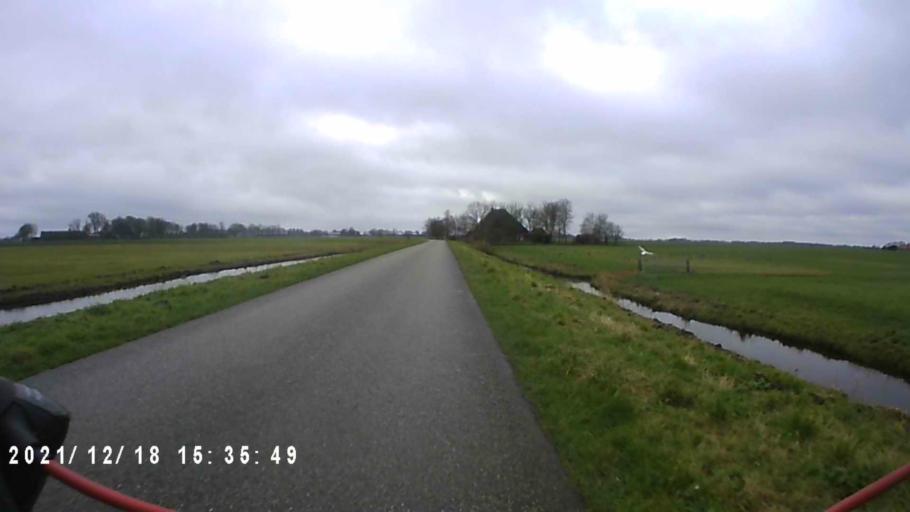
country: NL
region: Friesland
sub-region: Gemeente Dongeradeel
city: Anjum
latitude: 53.3424
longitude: 6.1305
